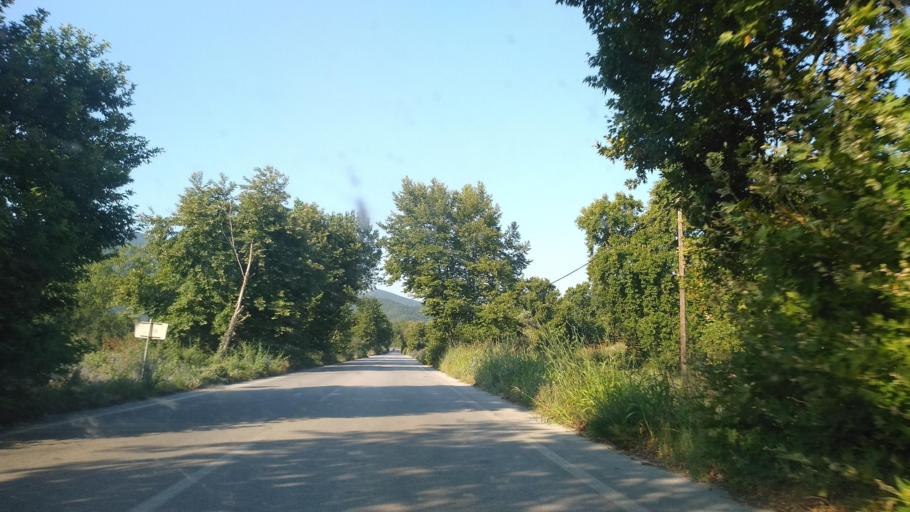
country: GR
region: Central Macedonia
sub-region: Nomos Thessalonikis
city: Nea Vrasna
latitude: 40.6857
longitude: 23.6781
